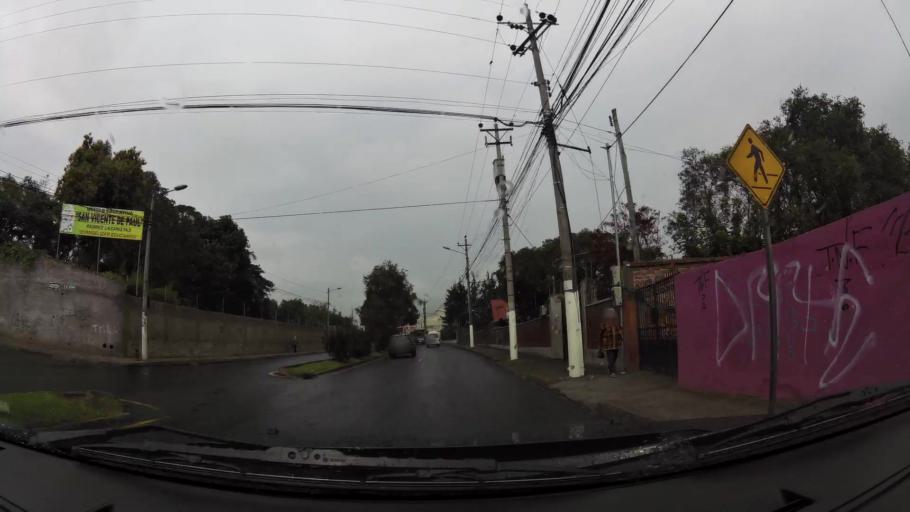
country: EC
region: Pichincha
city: Sangolqui
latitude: -0.2885
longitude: -78.4755
